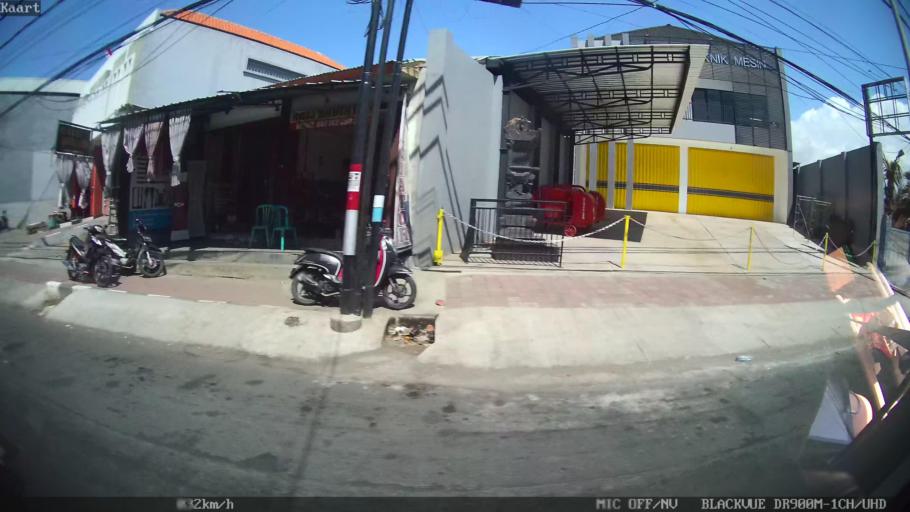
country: ID
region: Bali
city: Banjar Galiran
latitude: -8.1236
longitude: 115.0697
